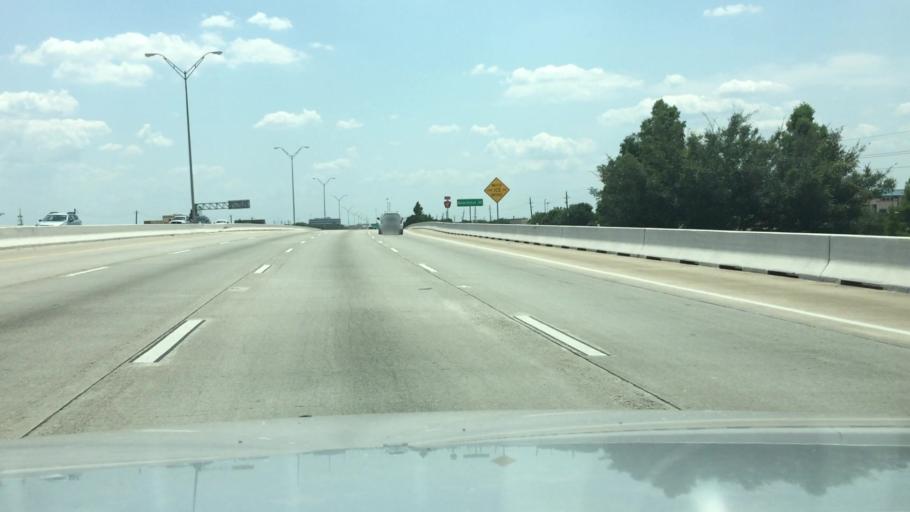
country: US
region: Texas
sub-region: Fort Bend County
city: Meadows Place
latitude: 29.6907
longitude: -95.5574
